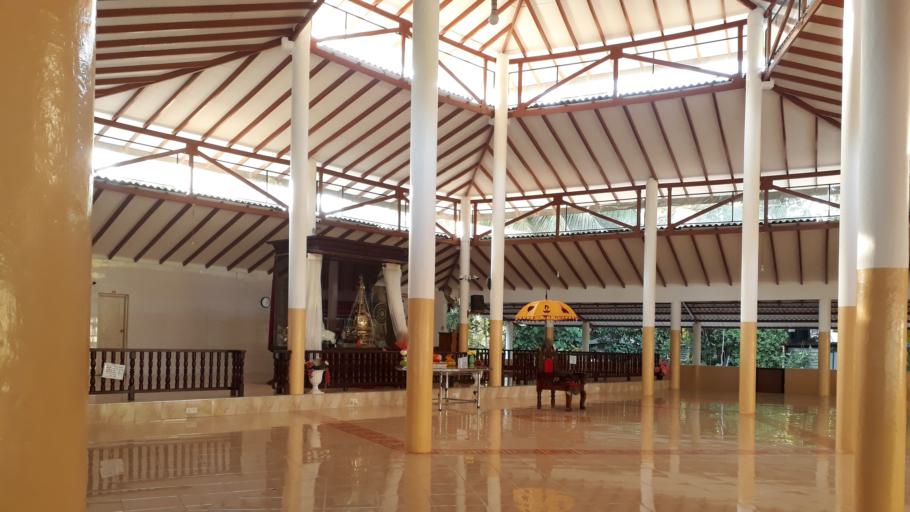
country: LK
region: Central
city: Dambulla
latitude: 7.7403
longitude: 80.5153
